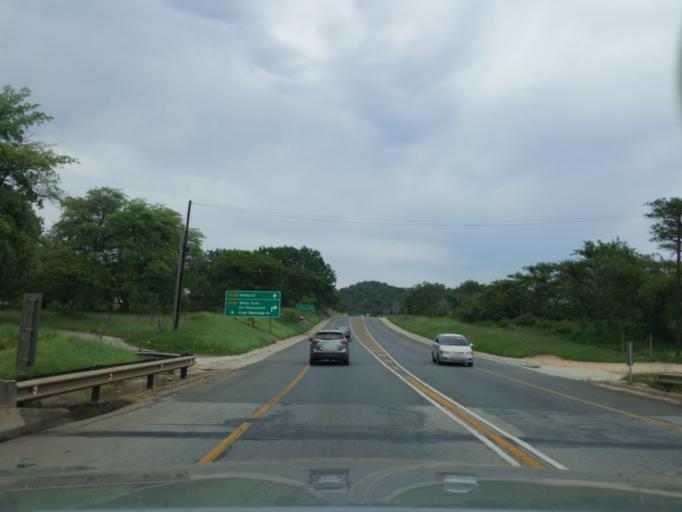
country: ZA
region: Mpumalanga
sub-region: Ehlanzeni District
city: Nelspruit
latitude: -25.4731
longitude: 31.0970
